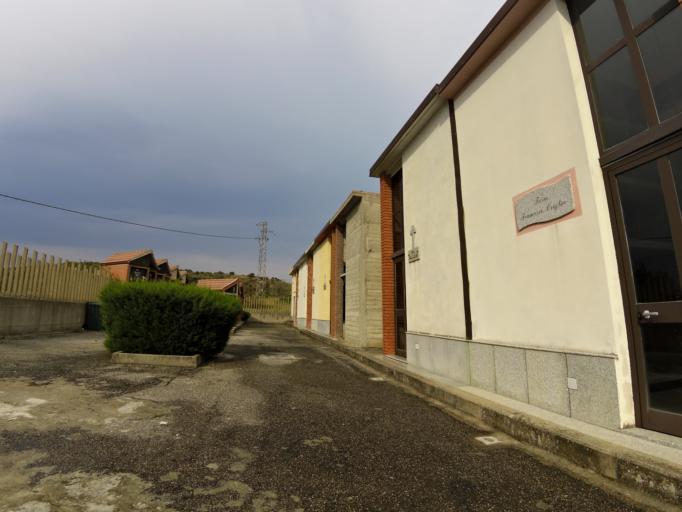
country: IT
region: Calabria
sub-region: Provincia di Reggio Calabria
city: Stignano
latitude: 38.4229
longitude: 16.4669
